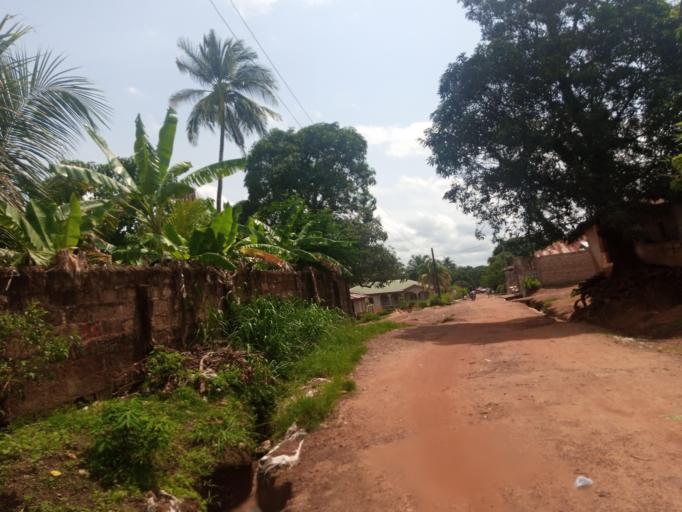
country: SL
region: Southern Province
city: Bo
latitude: 7.9725
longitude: -11.7331
